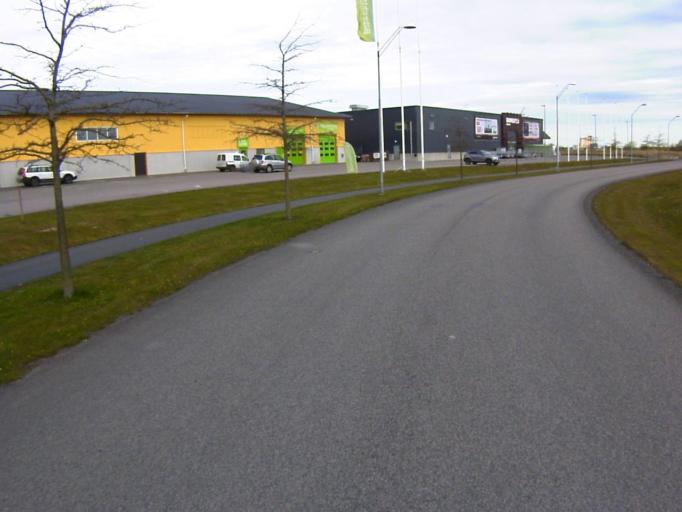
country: SE
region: Skane
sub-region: Kristianstads Kommun
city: Kristianstad
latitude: 56.0233
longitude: 14.1172
